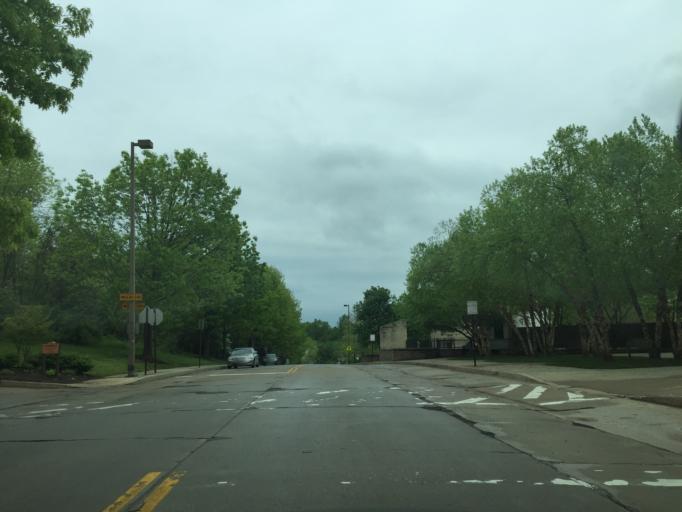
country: US
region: Maryland
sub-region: Baltimore County
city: Lochearn
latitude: 39.3469
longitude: -76.6549
